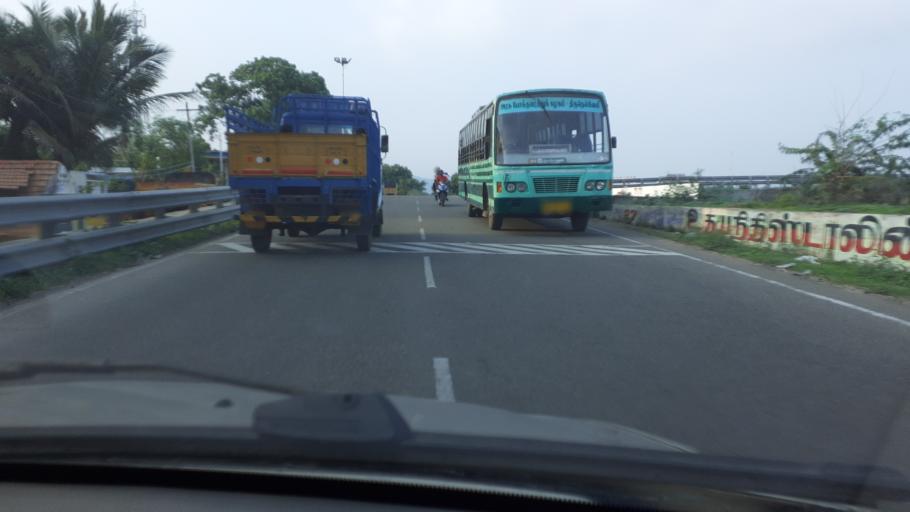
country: IN
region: Tamil Nadu
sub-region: Thoothukkudi
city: Srivaikuntam
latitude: 8.6221
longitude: 77.9102
